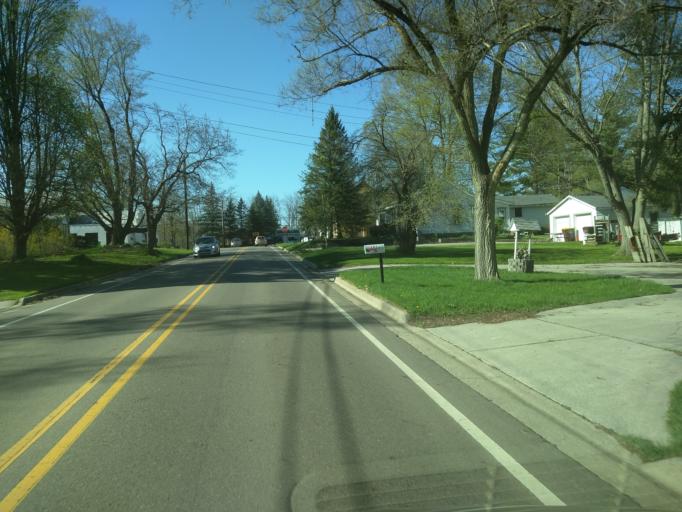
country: US
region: Michigan
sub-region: Eaton County
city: Waverly
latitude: 42.7639
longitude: -84.6503
